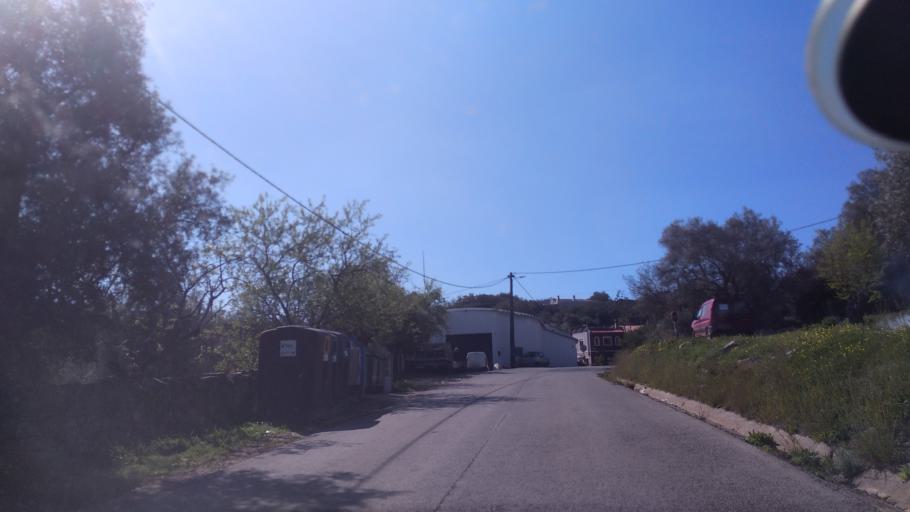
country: PT
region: Faro
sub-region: Faro
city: Santa Barbara de Nexe
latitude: 37.1180
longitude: -7.9262
